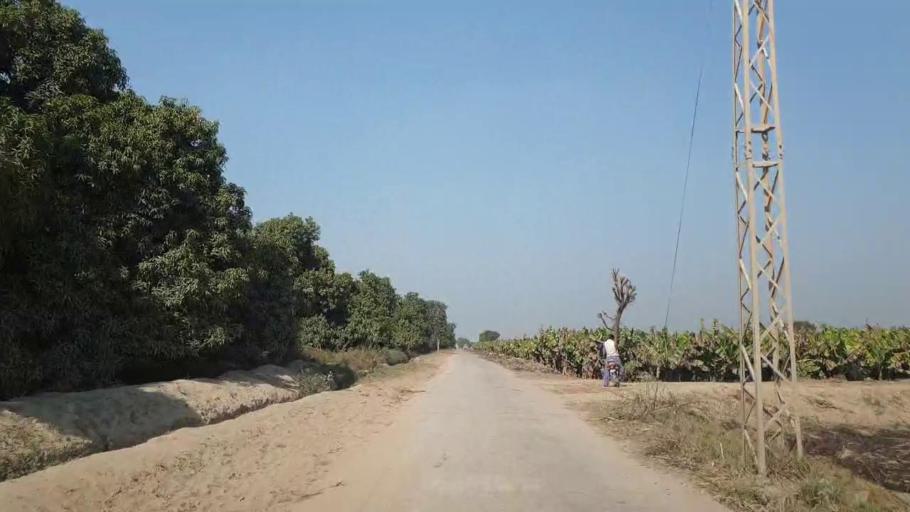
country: PK
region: Sindh
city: Tando Allahyar
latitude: 25.5030
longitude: 68.8221
